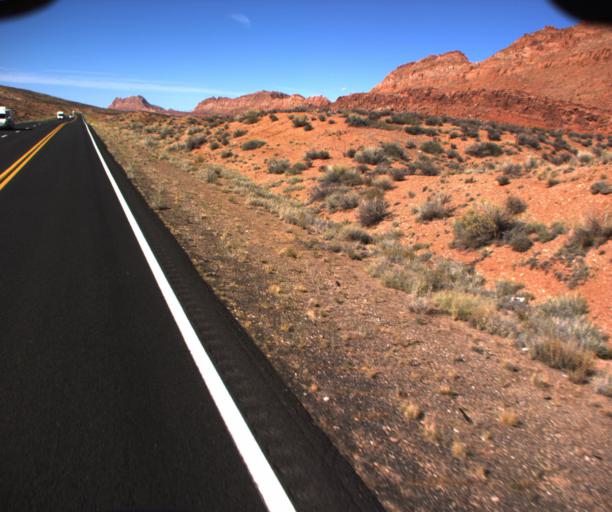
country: US
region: Arizona
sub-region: Coconino County
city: Tuba City
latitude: 36.2375
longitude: -111.4099
